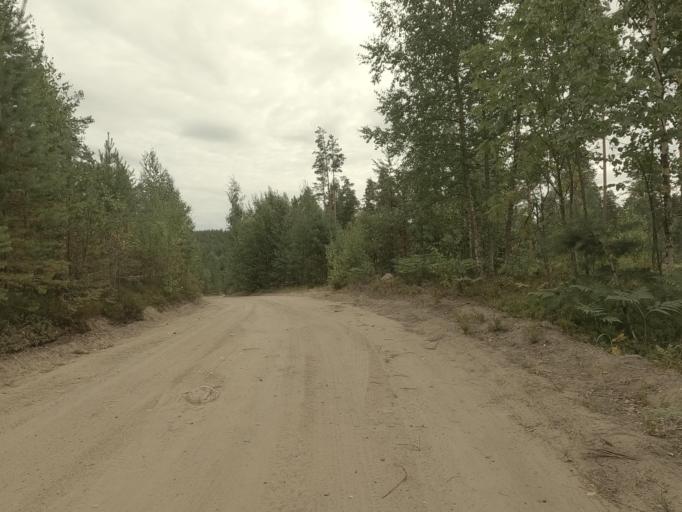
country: RU
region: Leningrad
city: Kamennogorsk
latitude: 61.0009
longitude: 29.1799
